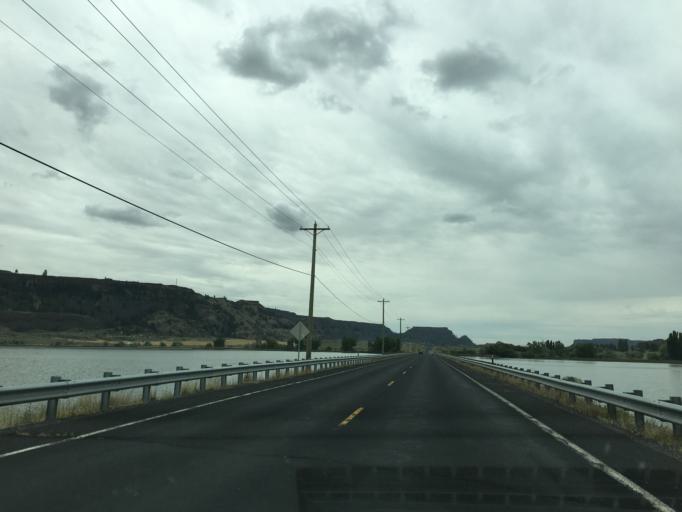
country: US
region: Washington
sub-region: Okanogan County
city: Coulee Dam
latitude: 47.9241
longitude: -119.0492
